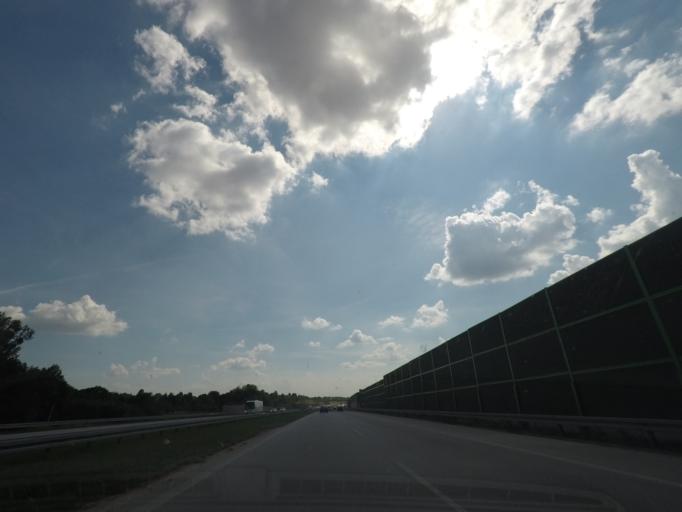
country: PL
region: Lodz Voivodeship
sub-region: Powiat zgierski
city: Strykow
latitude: 51.8272
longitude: 19.6517
